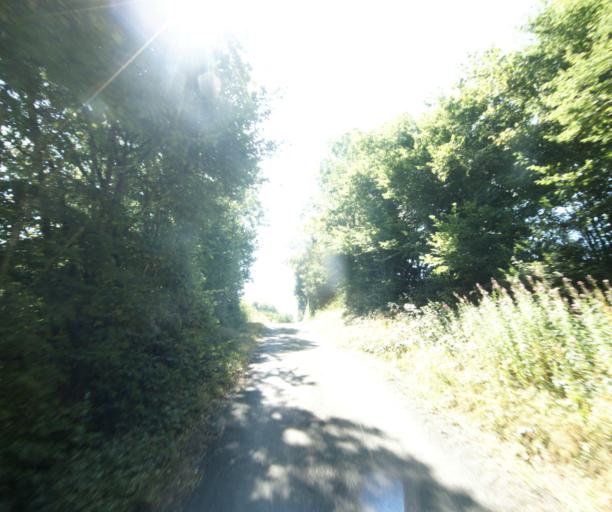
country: FR
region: Rhone-Alpes
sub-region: Departement du Rhone
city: Montrottier
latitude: 45.8070
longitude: 4.4954
